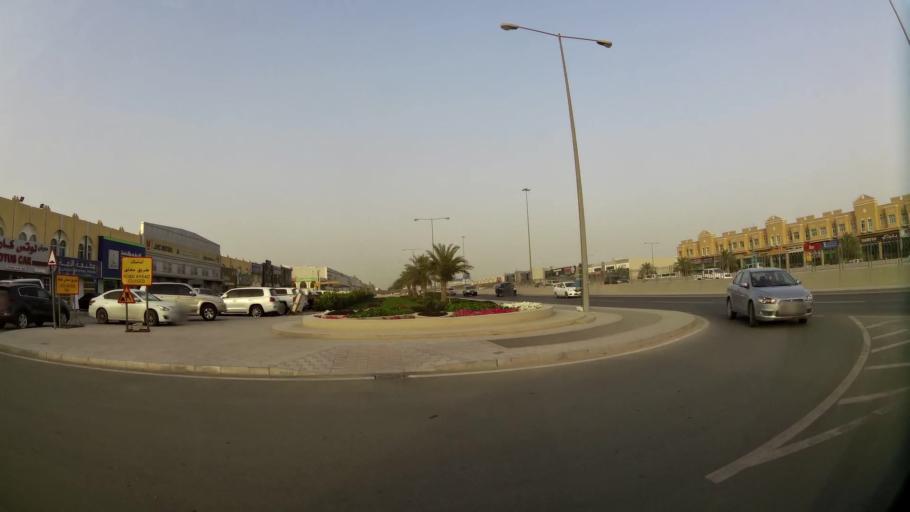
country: QA
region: Baladiyat ar Rayyan
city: Ar Rayyan
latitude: 25.2397
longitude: 51.4551
